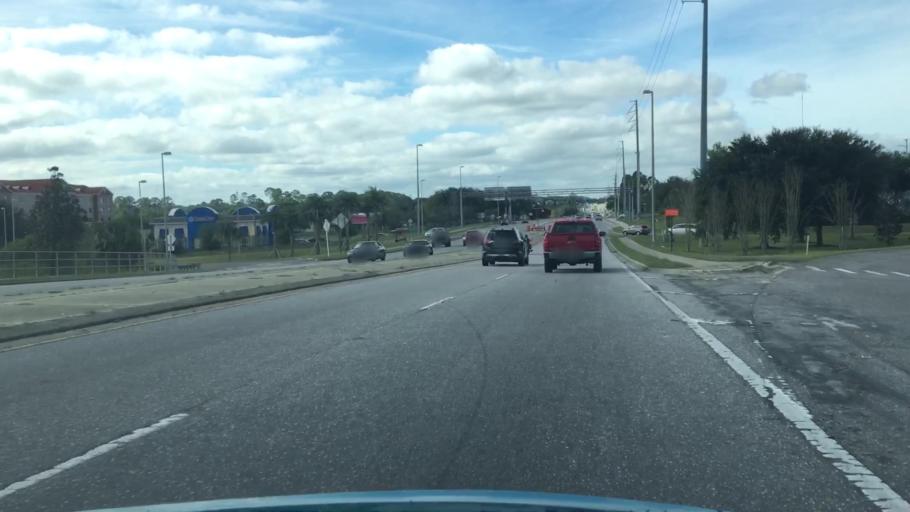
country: US
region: Florida
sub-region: Volusia County
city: Deltona
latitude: 28.9113
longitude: -81.2729
